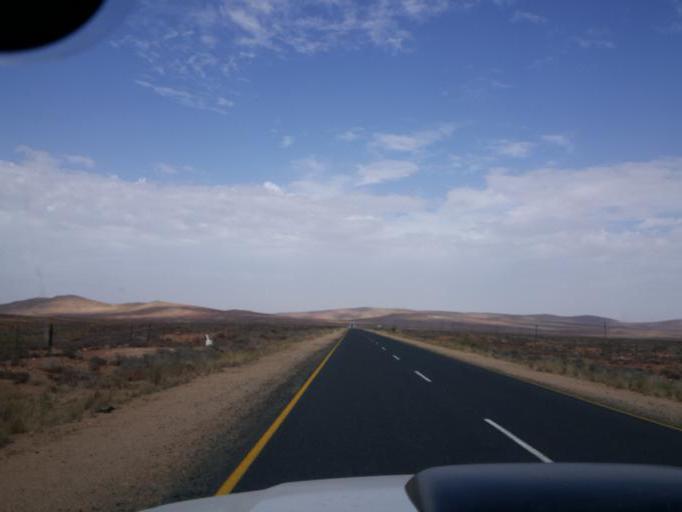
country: ZA
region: Northern Cape
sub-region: Namakwa District Municipality
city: Port Nolloth
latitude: -29.2596
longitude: 17.4518
